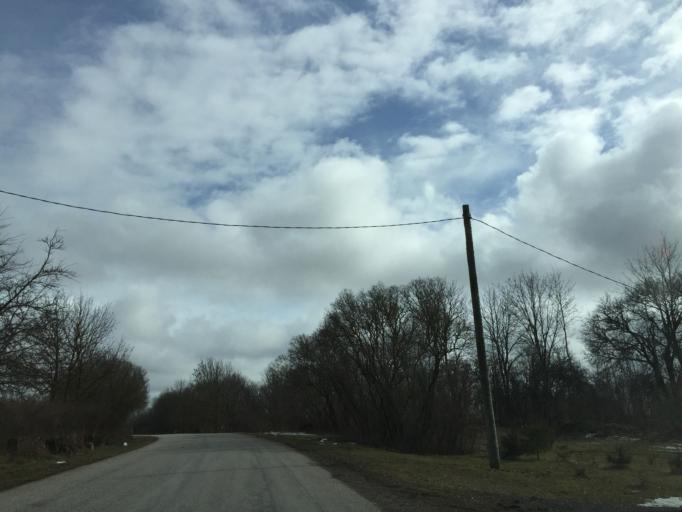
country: EE
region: Laeaene
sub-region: Lihula vald
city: Lihula
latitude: 58.7362
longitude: 23.8369
